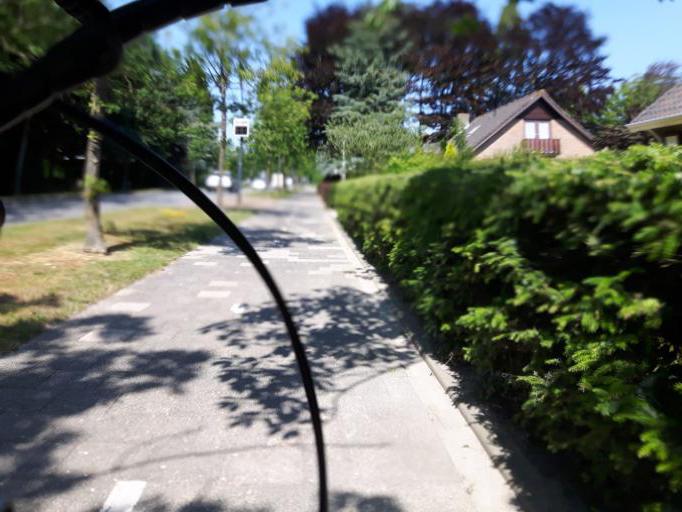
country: NL
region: Zeeland
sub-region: Gemeente Goes
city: Goes
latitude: 51.4788
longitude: 3.8169
